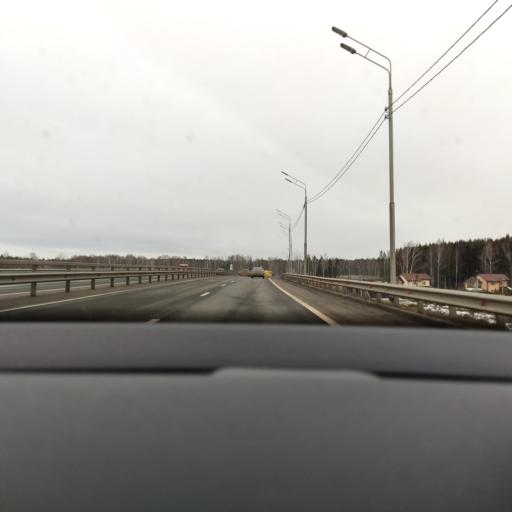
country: RU
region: Moskovskaya
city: Bol'shiye Vyazemy
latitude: 55.6454
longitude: 36.9902
